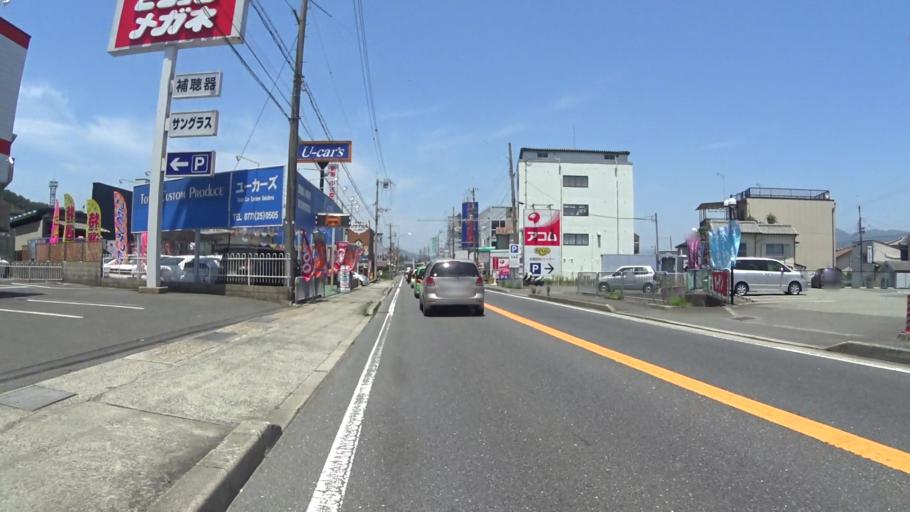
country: JP
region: Kyoto
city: Kameoka
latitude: 35.0099
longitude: 135.5760
